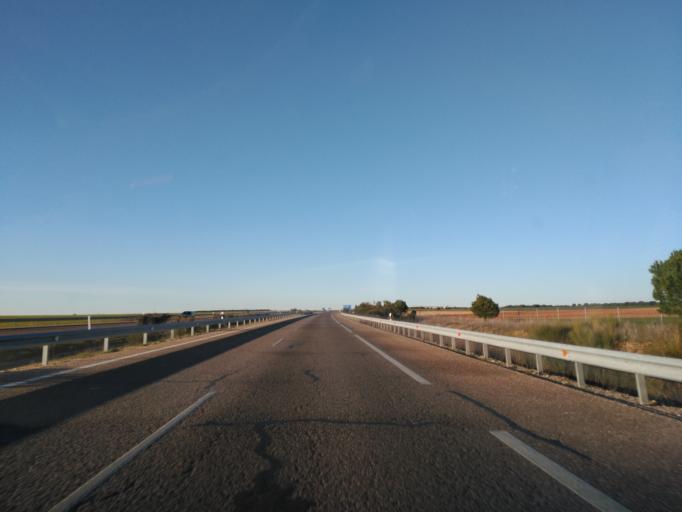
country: ES
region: Castille and Leon
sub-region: Provincia de Salamanca
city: Pajares de la Laguna
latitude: 41.1236
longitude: -5.4898
